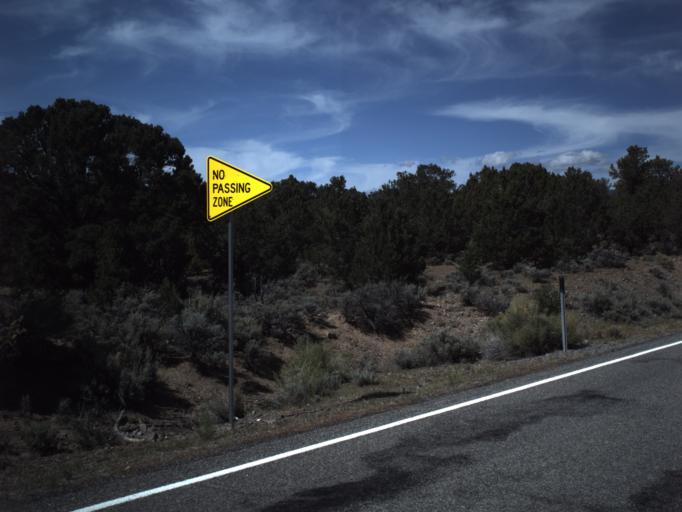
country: US
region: Utah
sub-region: Wayne County
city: Loa
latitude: 38.2106
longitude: -111.3477
